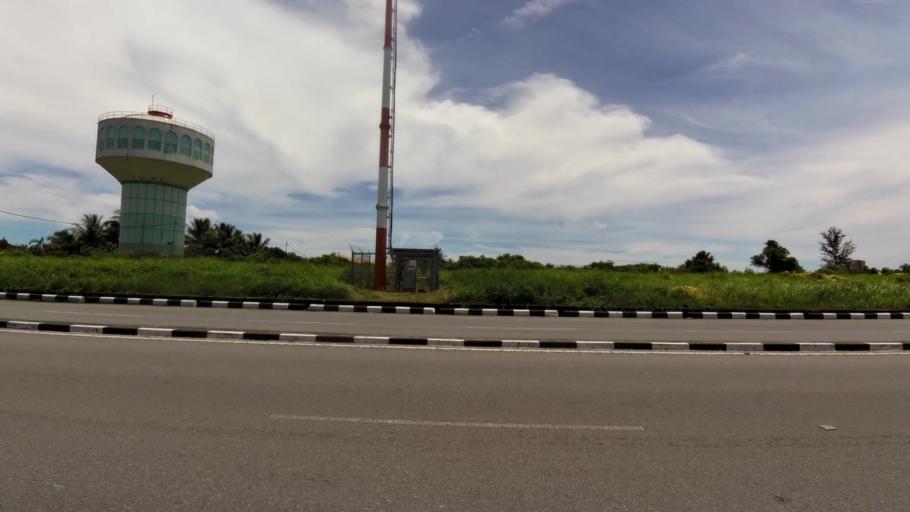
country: BN
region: Belait
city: Kuala Belait
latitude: 4.5850
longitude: 114.2443
